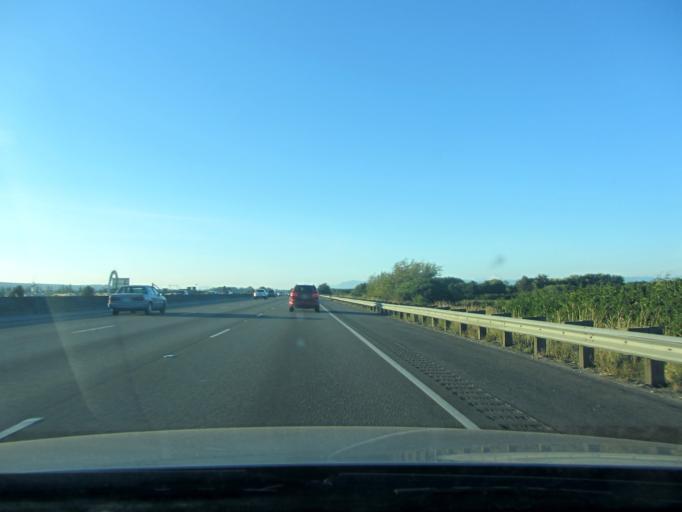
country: US
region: Washington
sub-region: Snohomish County
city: Marysville
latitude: 48.0146
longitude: -122.1743
